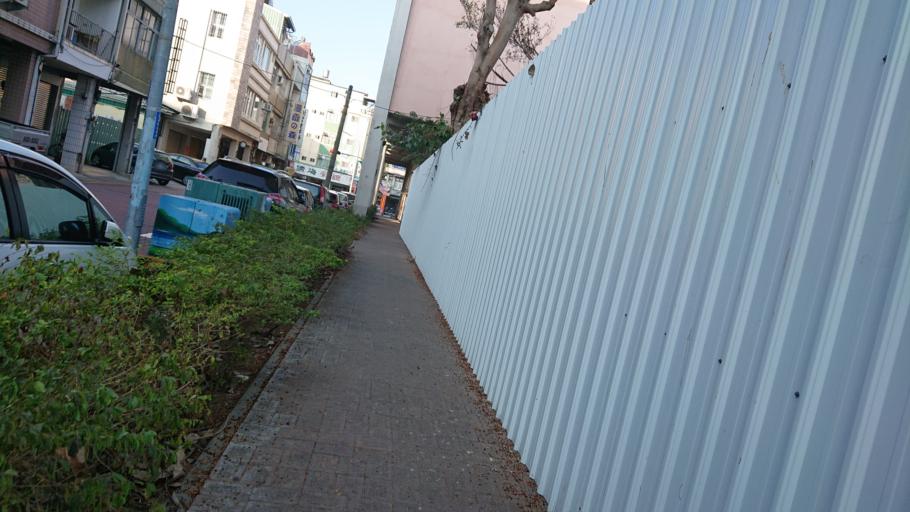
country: TW
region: Taiwan
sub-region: Tainan
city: Tainan
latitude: 22.9984
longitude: 120.2026
